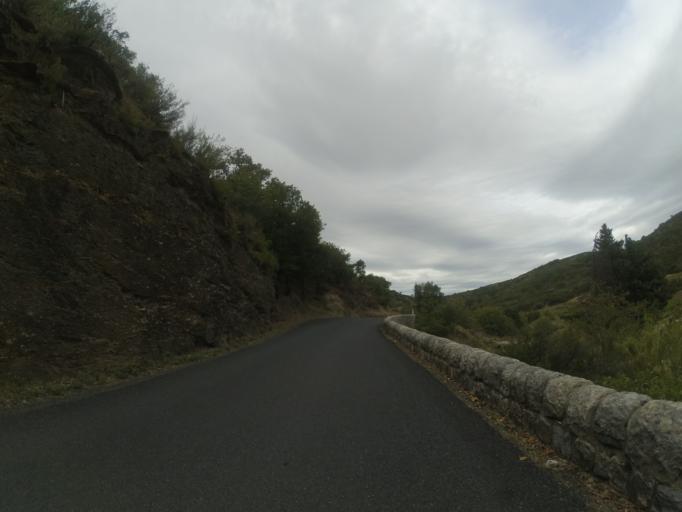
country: FR
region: Languedoc-Roussillon
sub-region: Departement des Pyrenees-Orientales
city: Estagel
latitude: 42.7645
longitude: 2.7039
